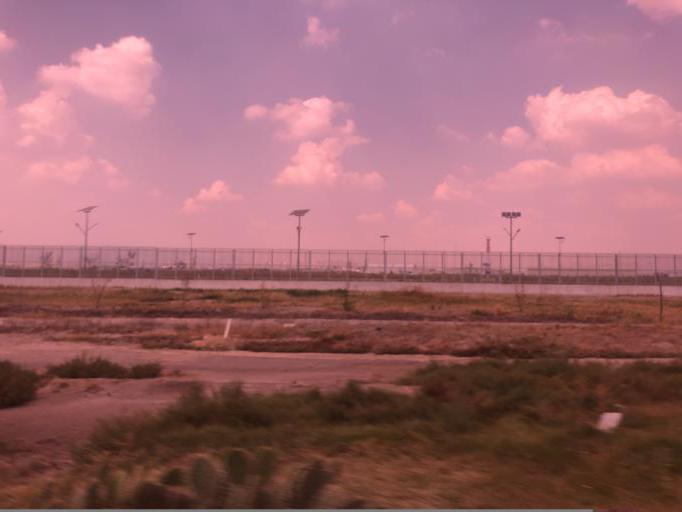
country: MX
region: Mexico
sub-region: Ciudad Nezahualcoyotl
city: Poligonos
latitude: 19.4767
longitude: -98.9848
